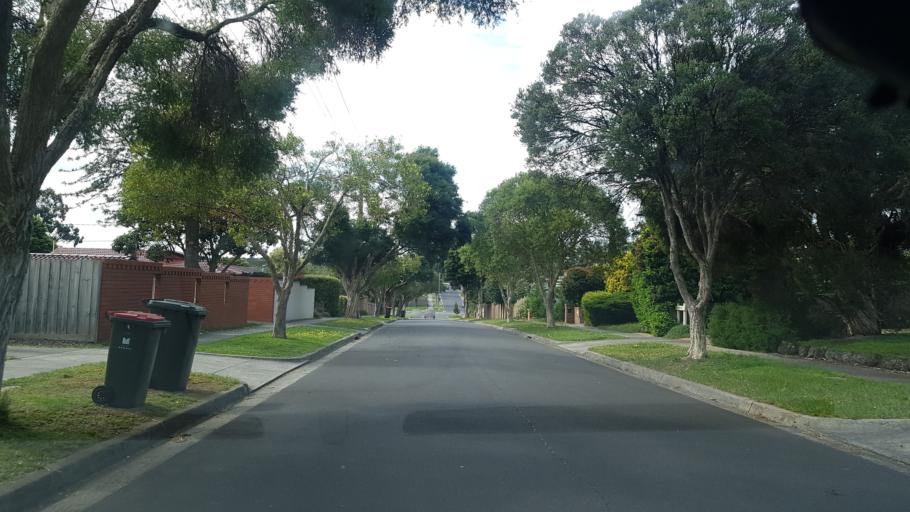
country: AU
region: Victoria
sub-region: Monash
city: Mulgrave
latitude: -37.9186
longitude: 145.1803
